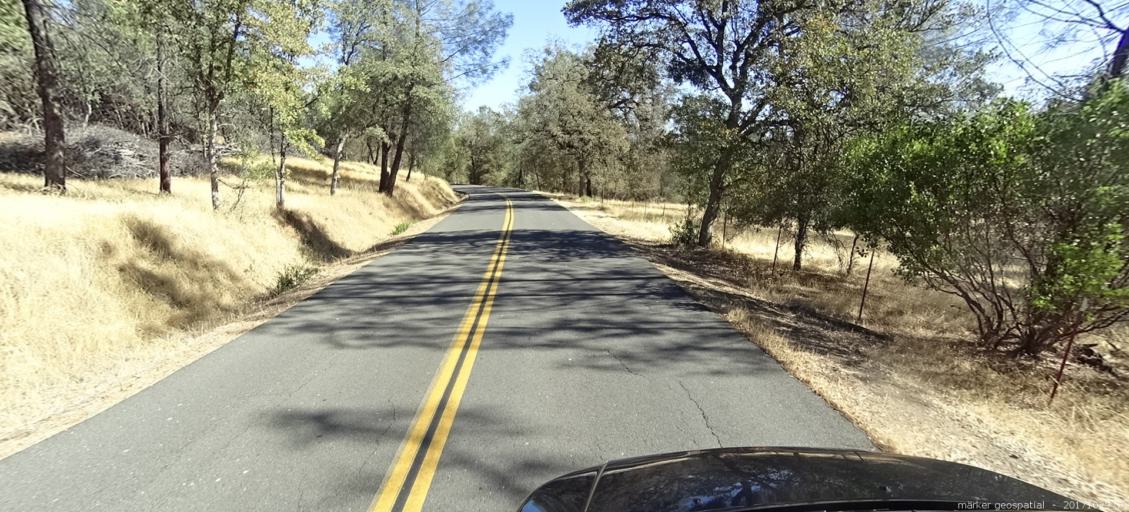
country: US
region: California
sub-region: Shasta County
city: Shasta
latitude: 40.4783
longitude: -122.6482
